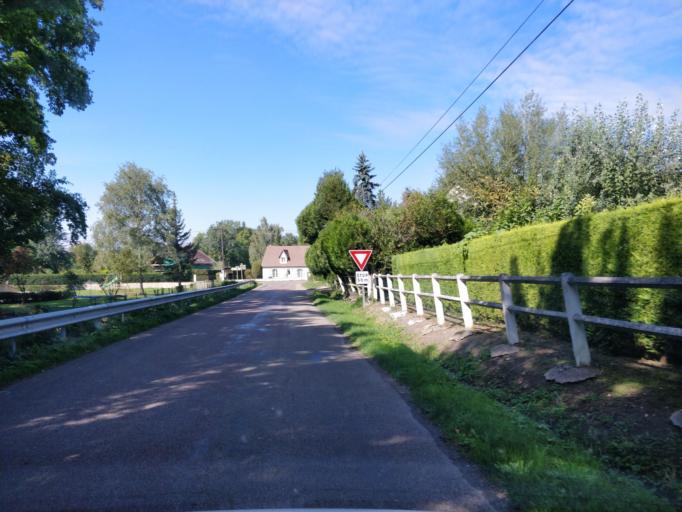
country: FR
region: Bourgogne
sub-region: Departement de l'Yonne
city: Saint-Florentin
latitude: 48.0265
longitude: 3.7415
